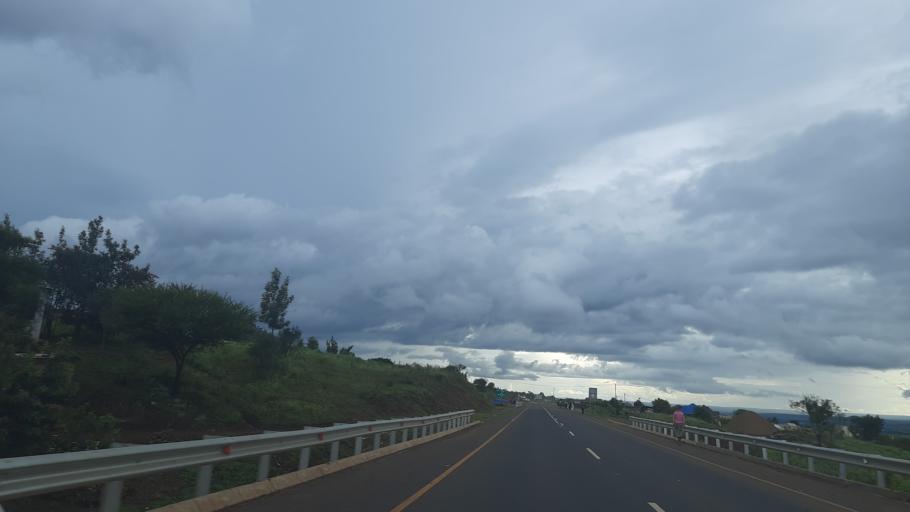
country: TZ
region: Arusha
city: Arusha
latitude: -3.4327
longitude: 36.6430
